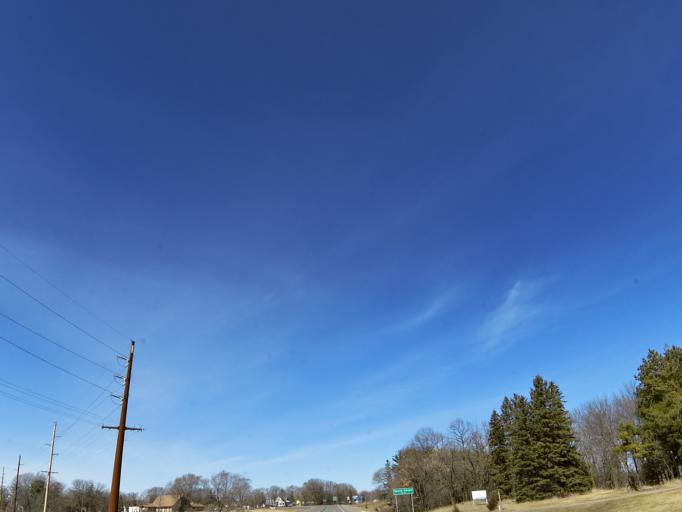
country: US
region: Minnesota
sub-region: Wright County
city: Annandale
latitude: 45.2902
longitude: -94.2087
